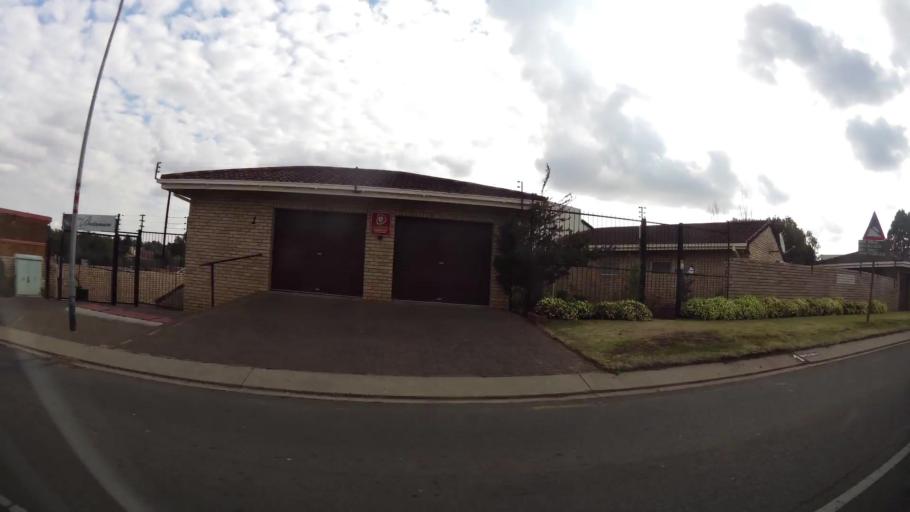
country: ZA
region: Orange Free State
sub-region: Mangaung Metropolitan Municipality
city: Bloemfontein
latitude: -29.0758
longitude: 26.2083
